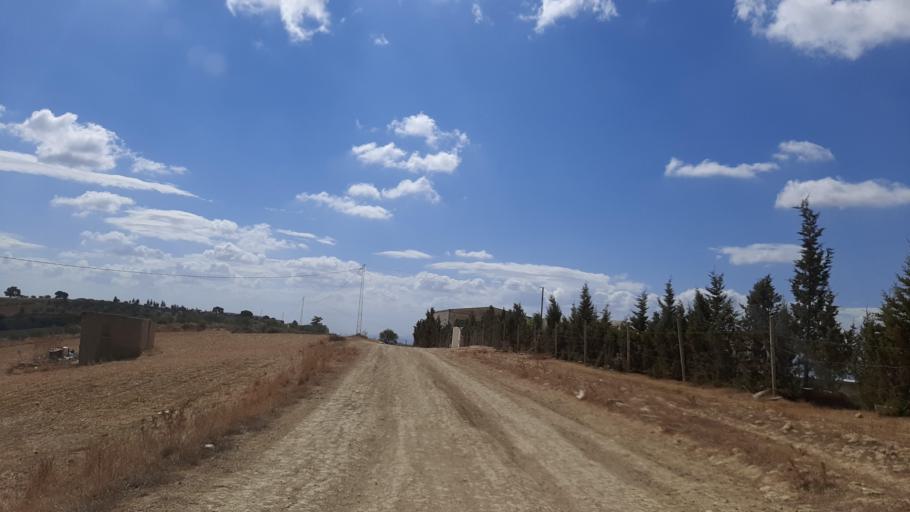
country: TN
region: Zaghwan
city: Zaghouan
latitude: 36.4888
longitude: 10.1775
